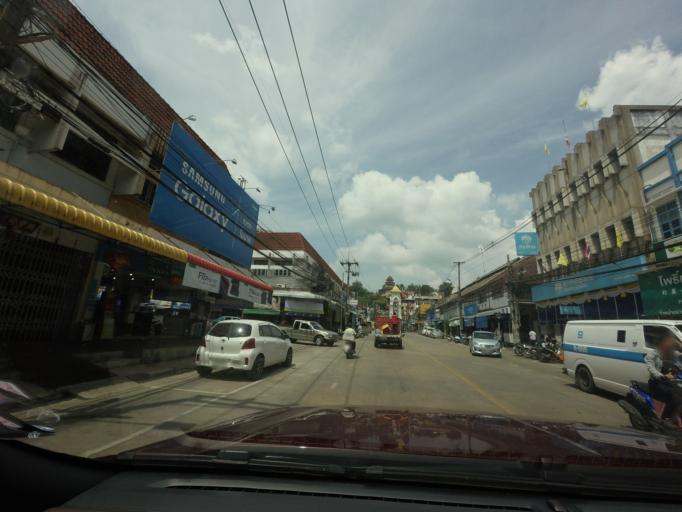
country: TH
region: Yala
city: Betong
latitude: 5.7727
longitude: 101.0716
